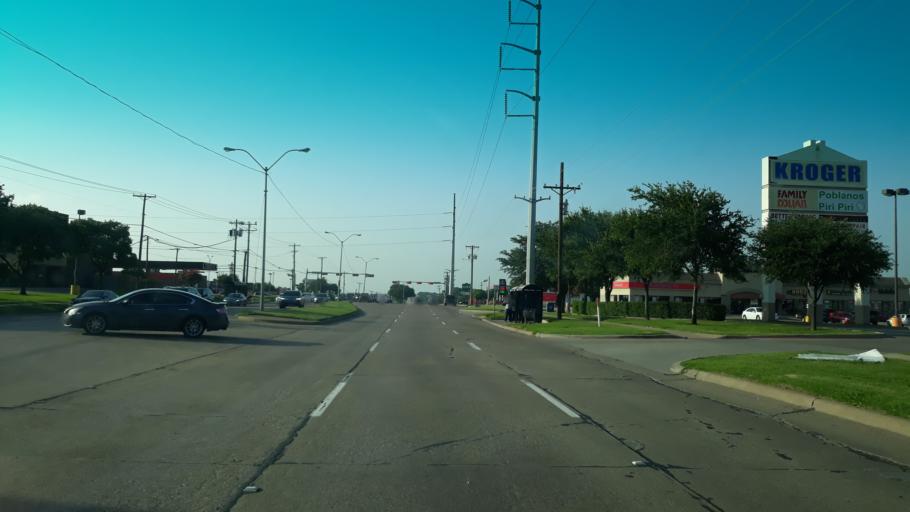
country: US
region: Texas
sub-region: Dallas County
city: Irving
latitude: 32.8553
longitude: -96.9921
